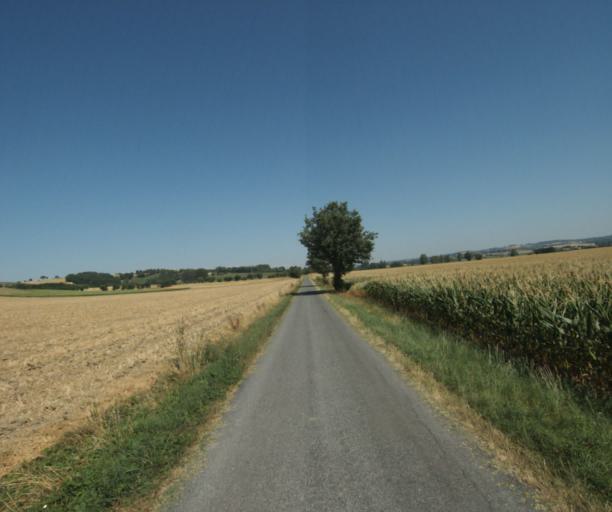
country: FR
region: Midi-Pyrenees
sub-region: Departement du Tarn
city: Puylaurens
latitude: 43.5213
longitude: 1.9426
